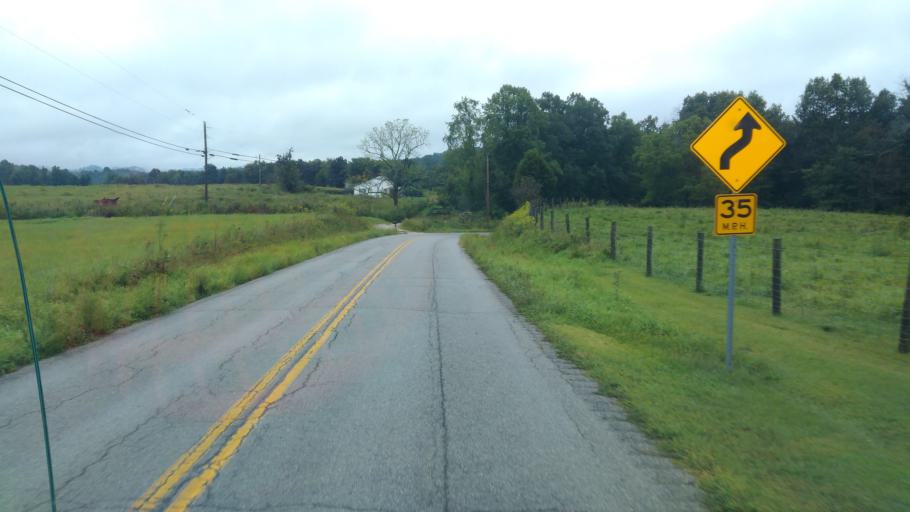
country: US
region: Kentucky
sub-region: Fleming County
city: Flemingsburg
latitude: 38.4551
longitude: -83.5212
